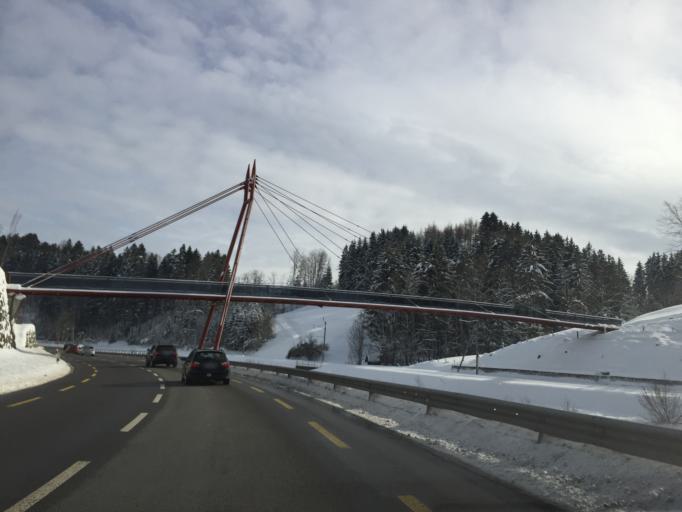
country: CH
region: Schwyz
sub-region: Bezirk Einsiedeln
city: Einsiedeln
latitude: 47.1504
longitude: 8.7325
